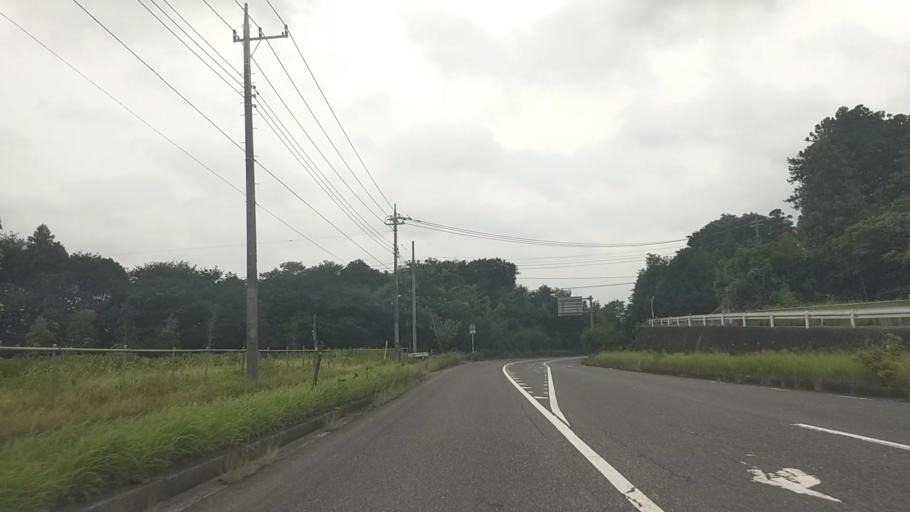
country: JP
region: Chiba
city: Kisarazu
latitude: 35.3848
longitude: 140.0050
